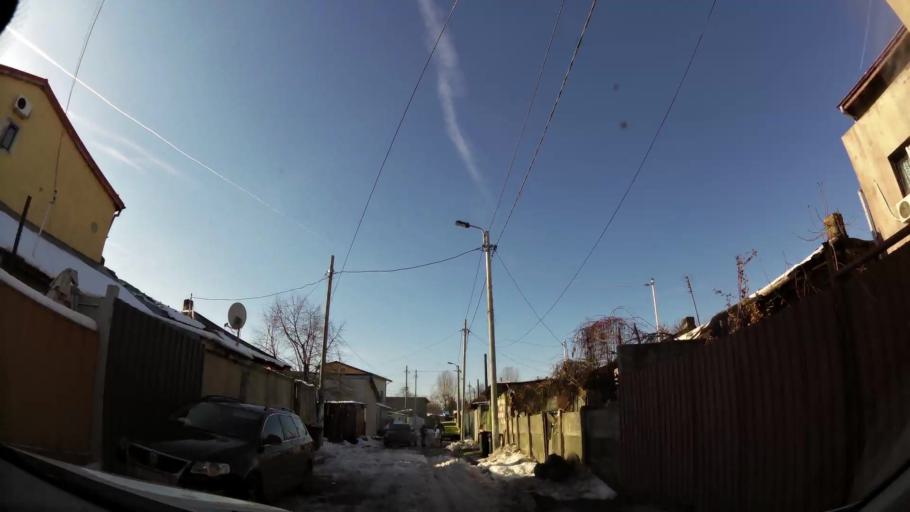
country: RO
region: Ilfov
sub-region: Comuna Fundeni-Dobroesti
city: Fundeni
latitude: 44.4721
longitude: 26.1304
